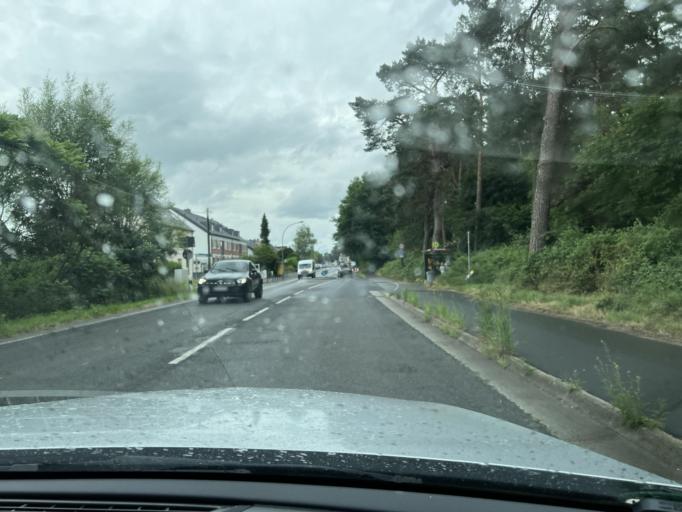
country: DE
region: North Rhine-Westphalia
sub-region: Regierungsbezirk Koln
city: Rath
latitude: 50.9398
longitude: 7.0865
